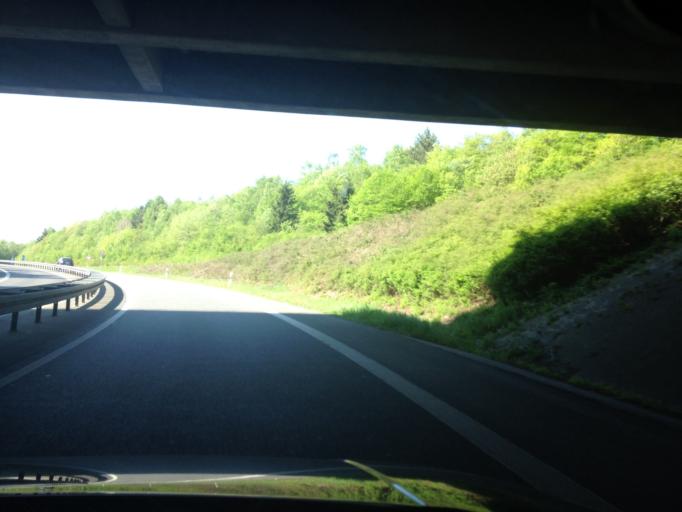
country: DE
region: Saarland
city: Friedrichsthal
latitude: 49.3210
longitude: 7.0796
